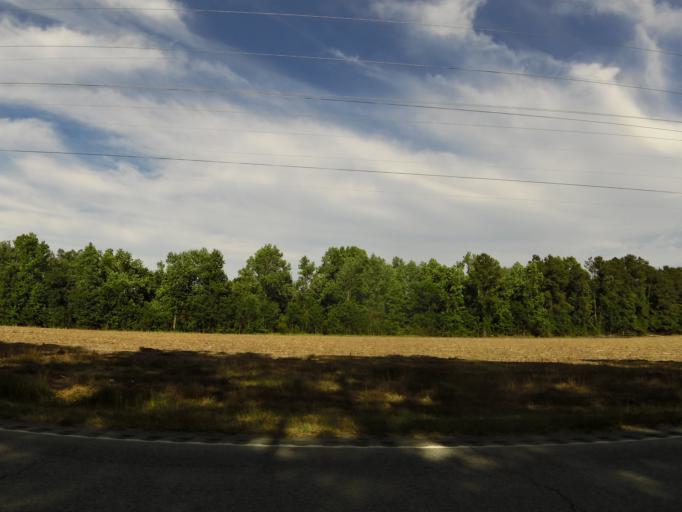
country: US
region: South Carolina
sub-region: Allendale County
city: Fairfax
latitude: 32.9350
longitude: -81.2371
